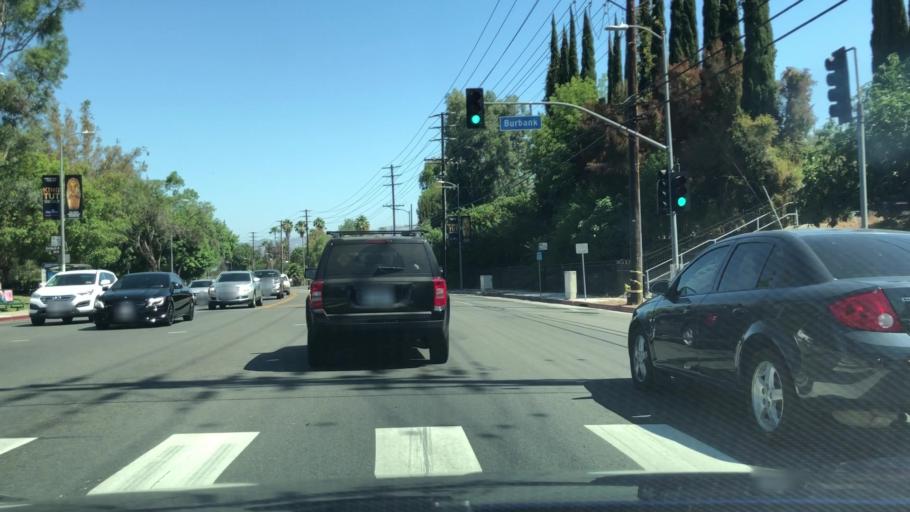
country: US
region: California
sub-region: Los Angeles County
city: Woodland Hills
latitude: 34.1732
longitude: -118.5882
